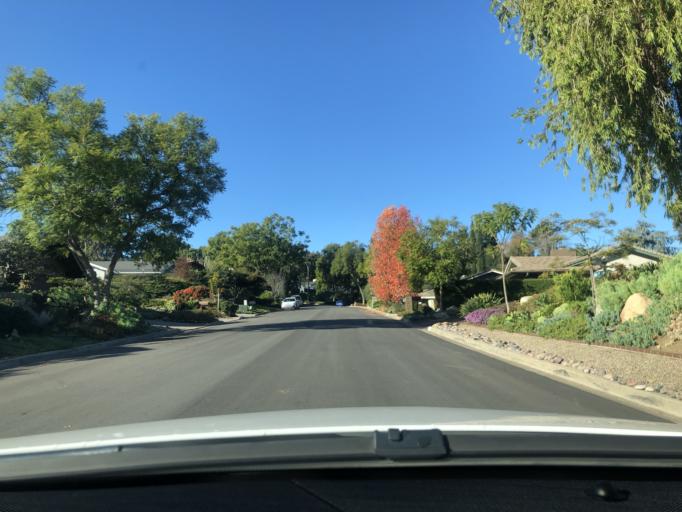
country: US
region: California
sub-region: San Diego County
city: Casa de Oro-Mount Helix
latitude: 32.7708
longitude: -116.9599
